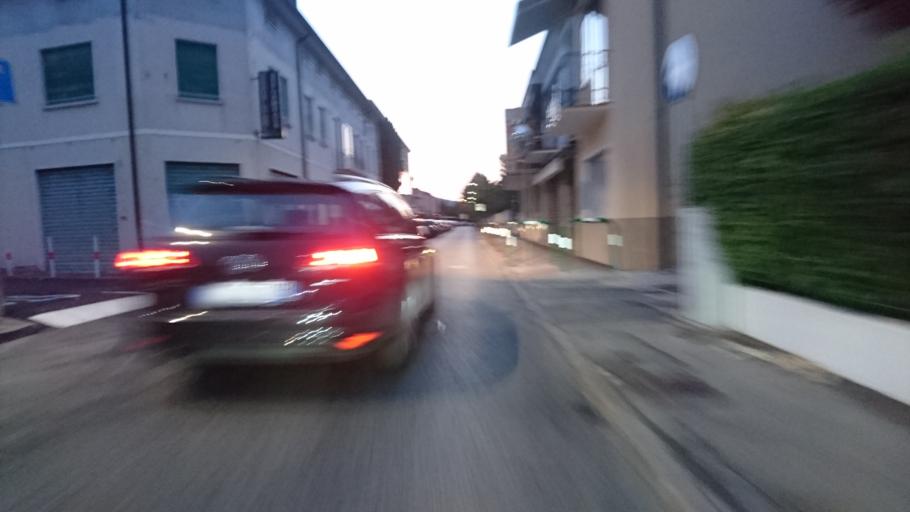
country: IT
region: Veneto
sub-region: Provincia di Padova
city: Abano Terme
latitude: 45.3505
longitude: 11.7774
